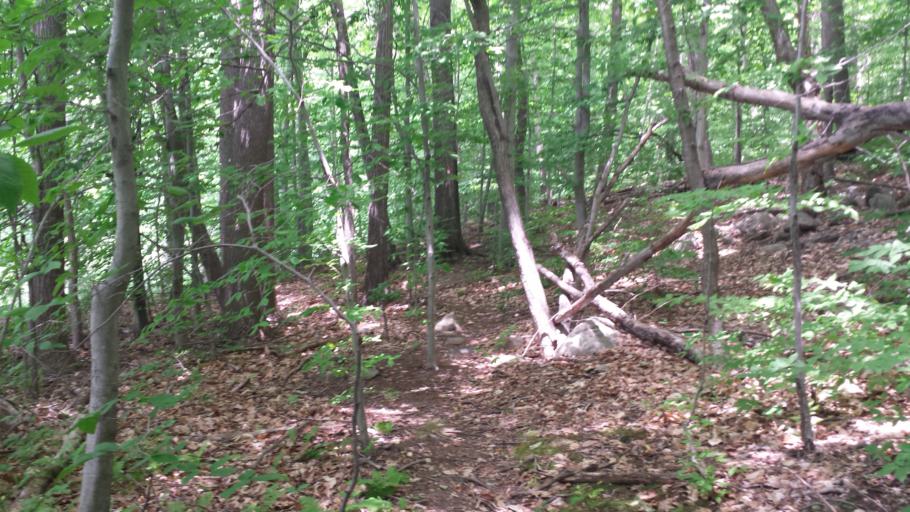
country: US
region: New York
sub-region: Putnam County
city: Peach Lake
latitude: 41.3113
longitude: -73.5677
